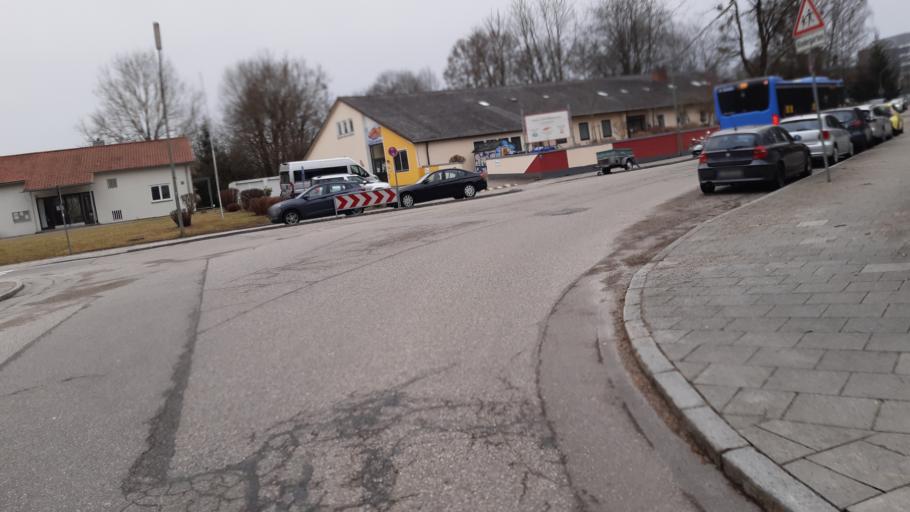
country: DE
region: Bavaria
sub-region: Upper Bavaria
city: Karlsfeld
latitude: 48.2139
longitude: 11.4866
